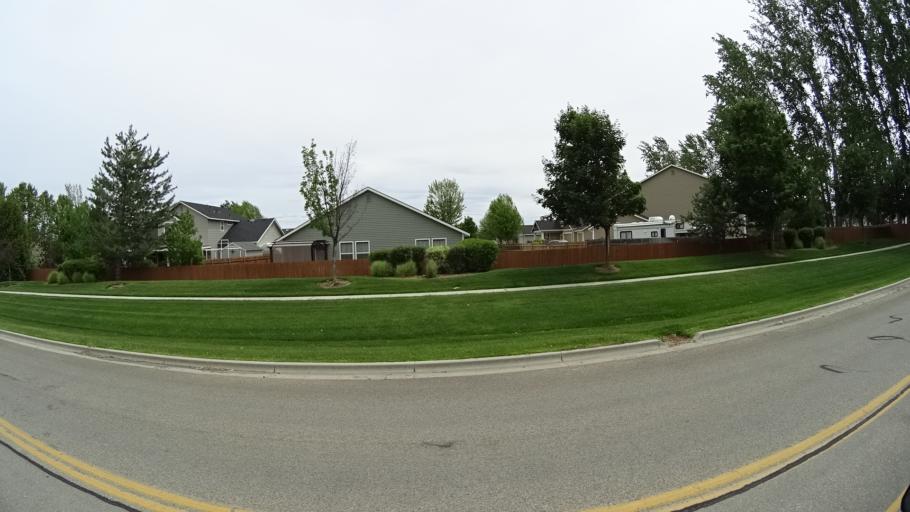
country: US
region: Idaho
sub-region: Ada County
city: Meridian
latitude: 43.5627
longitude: -116.3742
